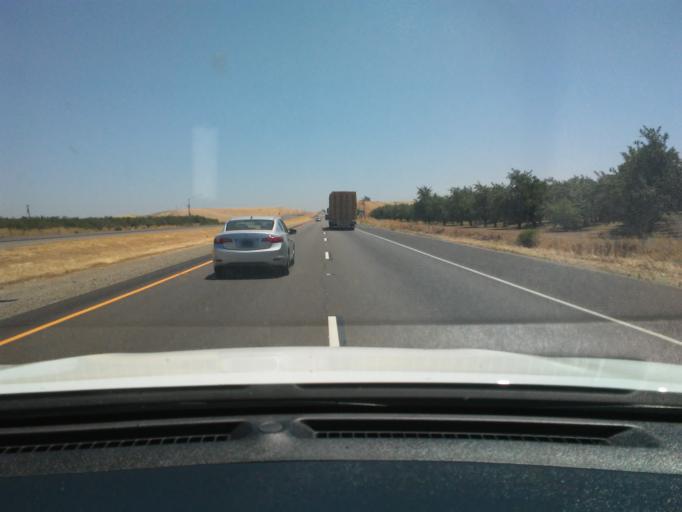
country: US
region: California
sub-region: Stanislaus County
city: Patterson
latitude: 37.4019
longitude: -121.1416
